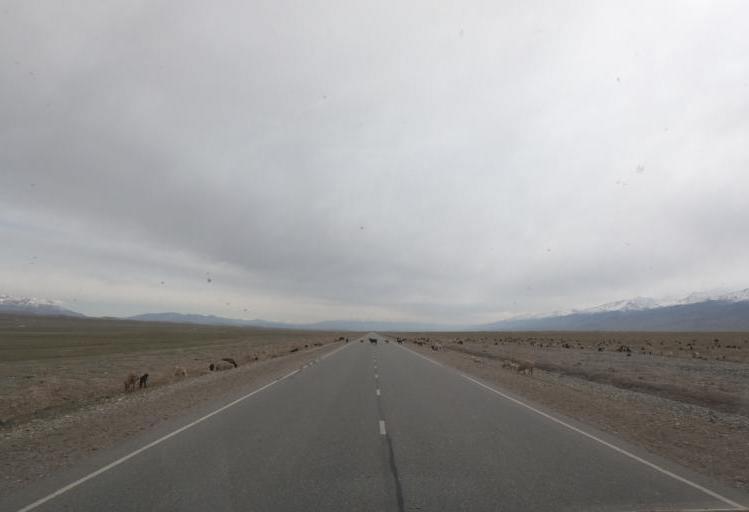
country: KG
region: Naryn
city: At-Bashi
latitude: 41.0545
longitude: 75.4922
